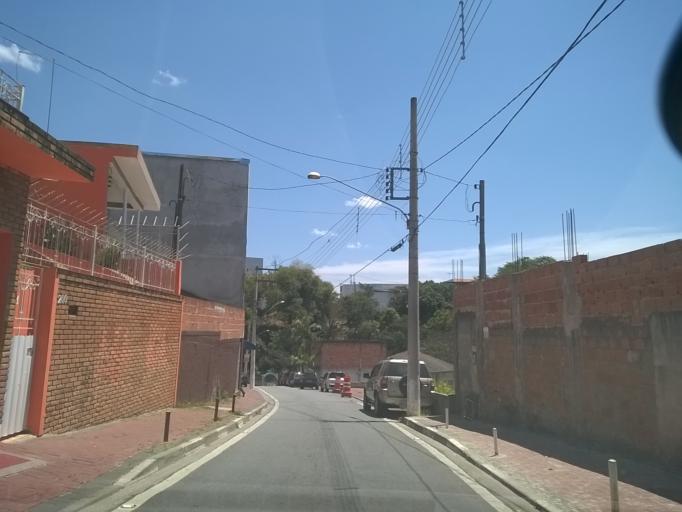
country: BR
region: Sao Paulo
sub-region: Francisco Morato
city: Francisco Morato
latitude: -23.2831
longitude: -46.7464
